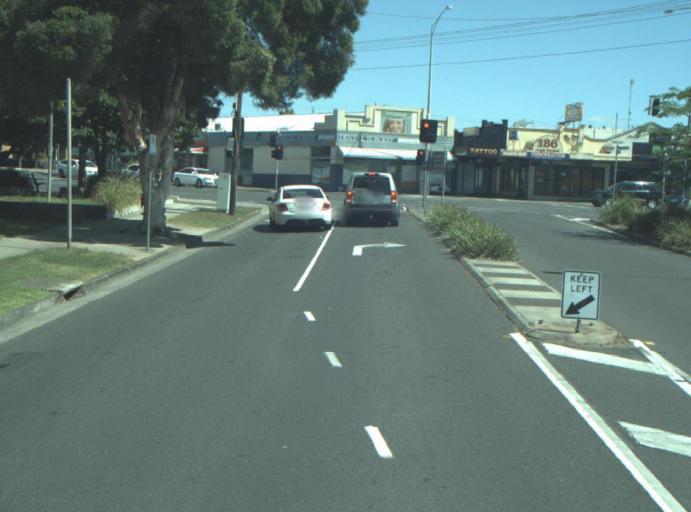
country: AU
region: Victoria
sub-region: Greater Geelong
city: Breakwater
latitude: -38.1758
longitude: 144.3429
